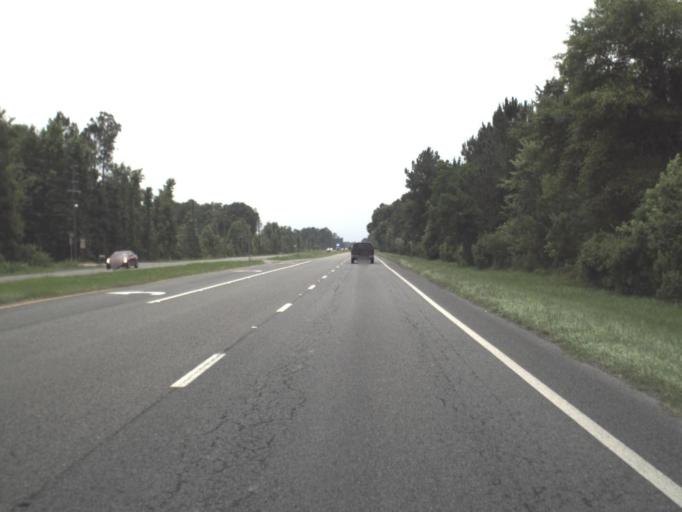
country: US
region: Florida
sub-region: Nassau County
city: Callahan
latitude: 30.6091
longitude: -81.8383
